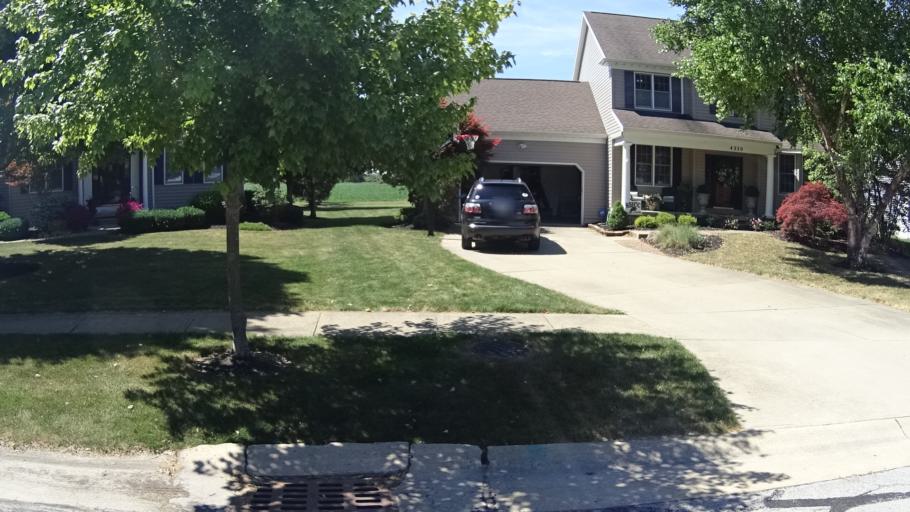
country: US
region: Ohio
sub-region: Erie County
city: Sandusky
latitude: 41.4047
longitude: -82.7018
